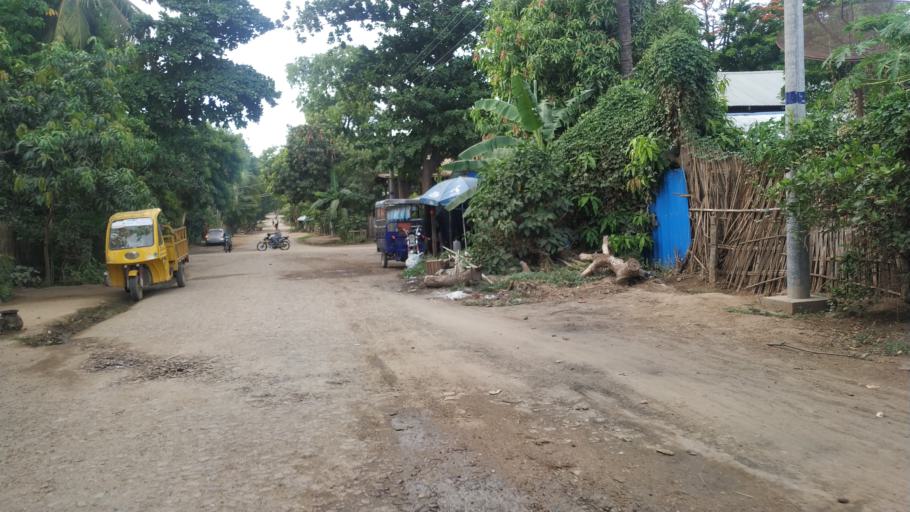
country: MM
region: Magway
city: Pakokku
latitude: 21.3351
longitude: 95.0713
